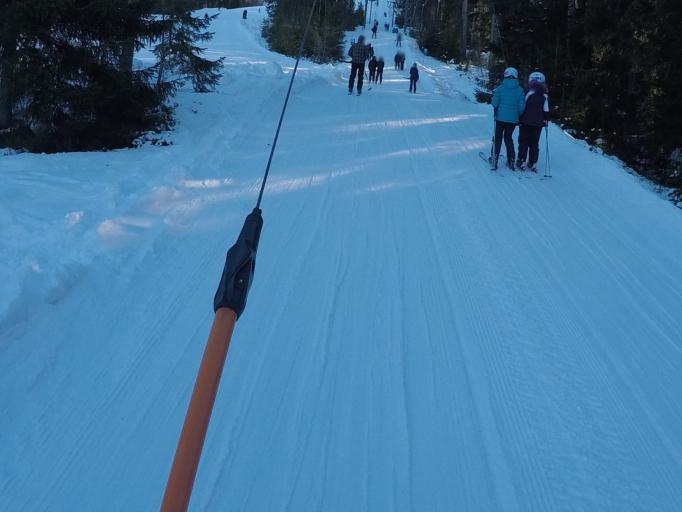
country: SE
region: Dalarna
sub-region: Borlange Kommun
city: Borlaenge
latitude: 60.3867
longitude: 15.3971
